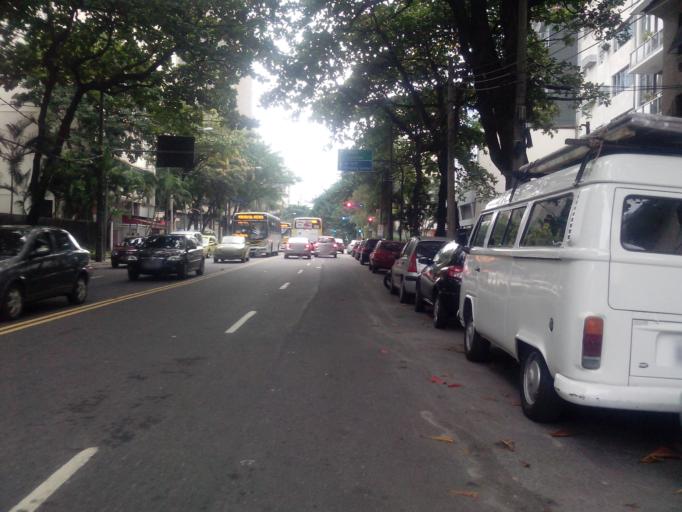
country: BR
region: Rio de Janeiro
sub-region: Rio De Janeiro
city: Rio de Janeiro
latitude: -22.9846
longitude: -43.2176
